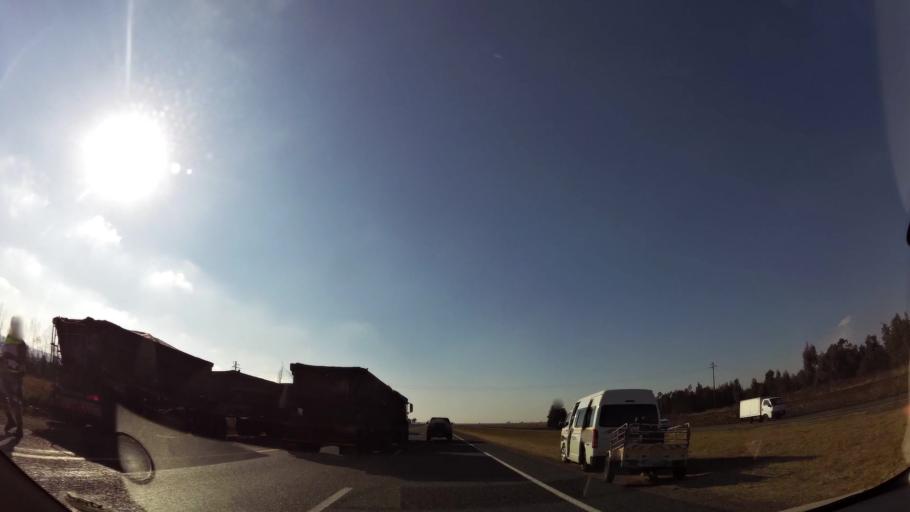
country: ZA
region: Mpumalanga
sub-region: Nkangala District Municipality
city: Delmas
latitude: -26.0190
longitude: 28.9173
